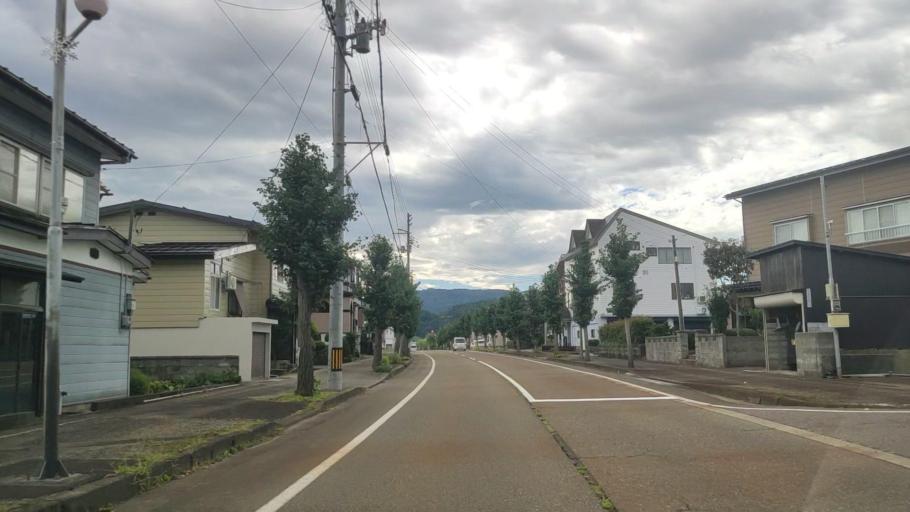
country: JP
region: Niigata
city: Arai
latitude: 37.0213
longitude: 138.2466
